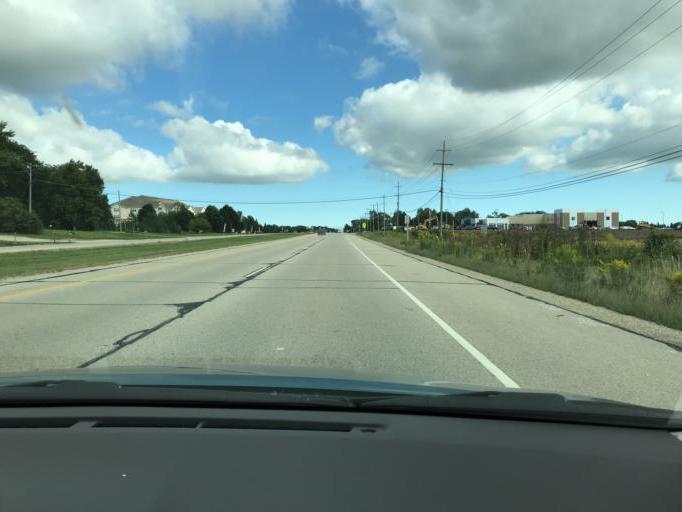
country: US
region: Wisconsin
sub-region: Kenosha County
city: Pleasant Prairie
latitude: 42.5673
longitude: -87.9444
